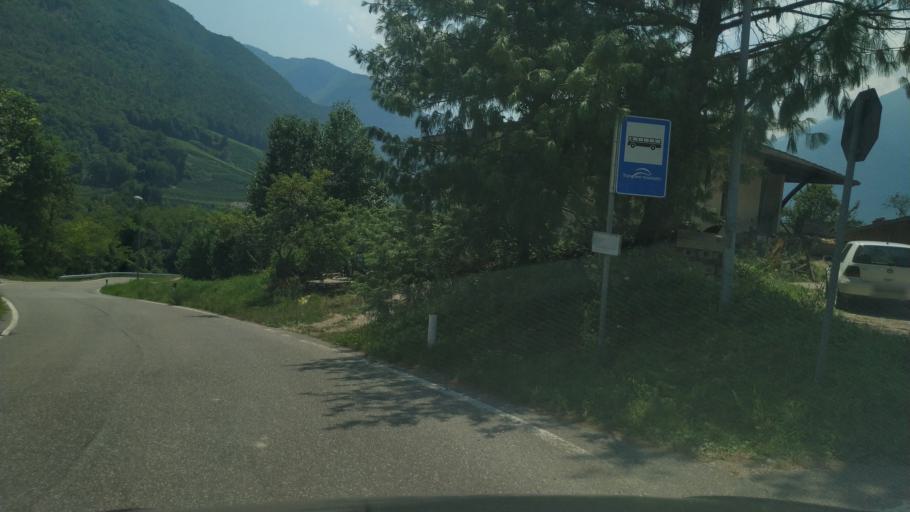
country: IT
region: Trentino-Alto Adige
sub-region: Provincia di Trento
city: Vigo di Ton
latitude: 46.2547
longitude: 11.0697
